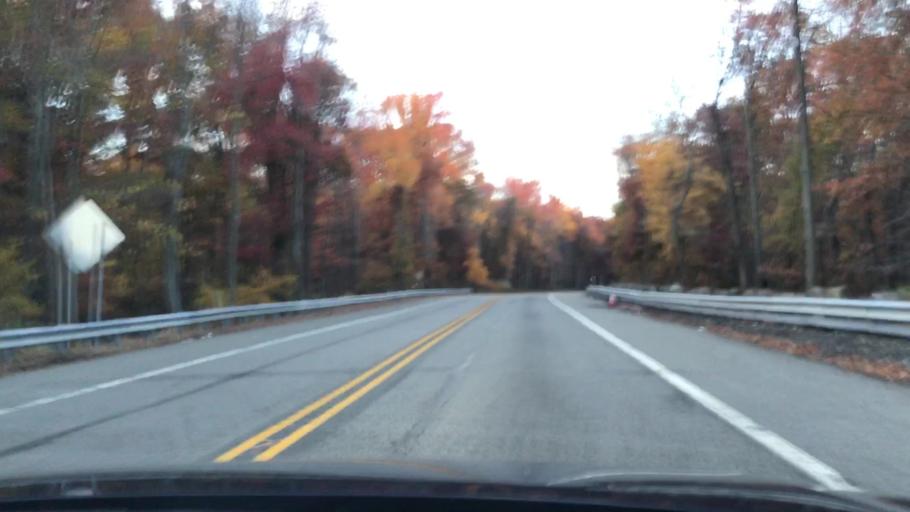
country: US
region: New Jersey
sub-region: Bergen County
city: Tenafly
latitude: 40.9175
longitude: -73.9366
